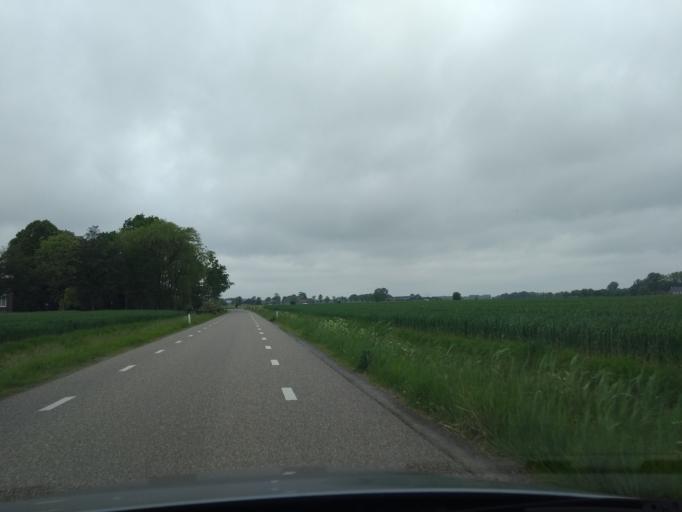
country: NL
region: Groningen
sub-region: Gemeente Zuidhorn
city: Oldehove
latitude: 53.3331
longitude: 6.4260
